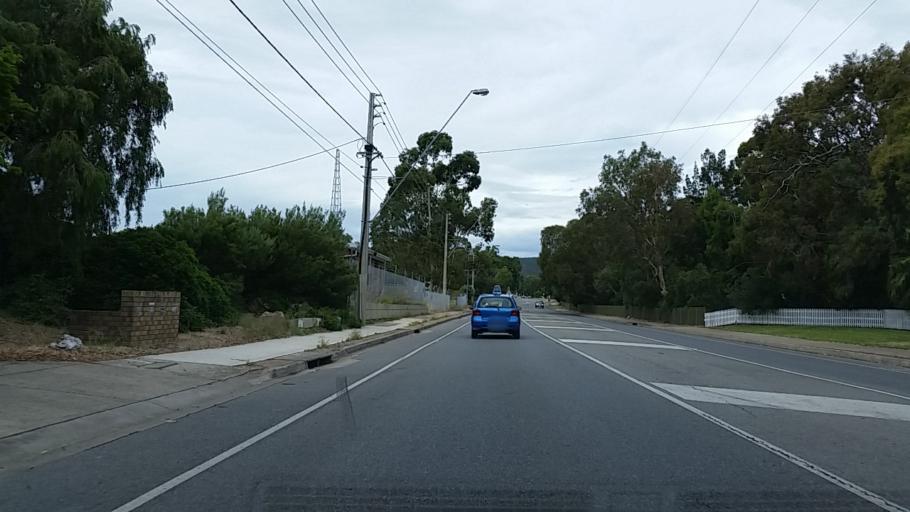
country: AU
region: South Australia
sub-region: Tea Tree Gully
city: Hope Valley
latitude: -34.8328
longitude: 138.6979
